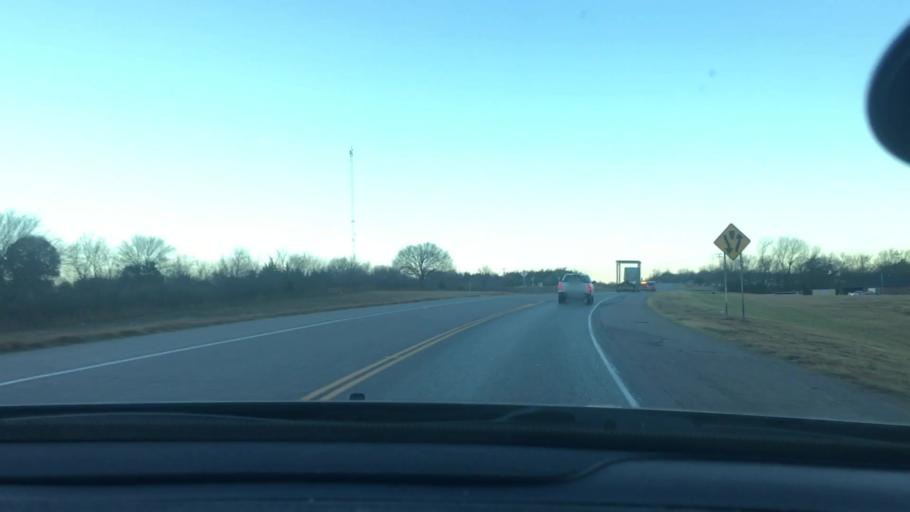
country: US
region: Oklahoma
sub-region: Pontotoc County
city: Ada
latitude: 34.7495
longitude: -96.7024
